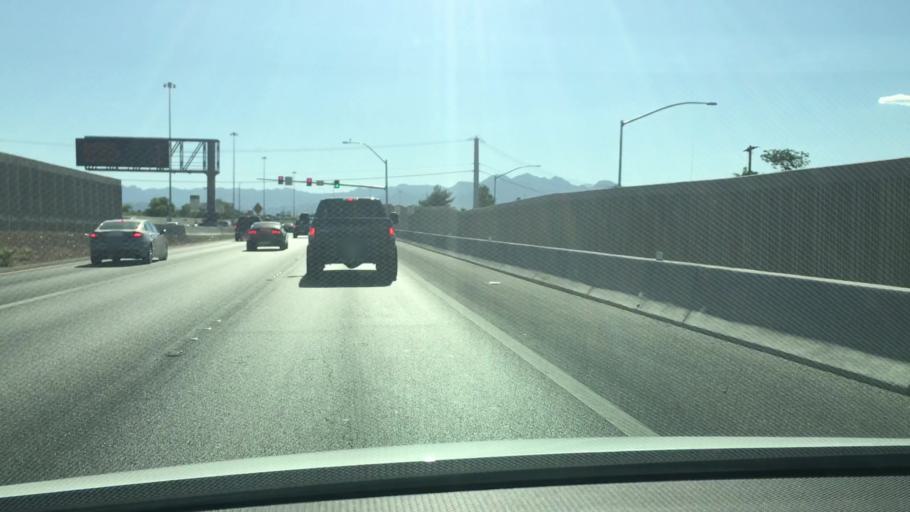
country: US
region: Nevada
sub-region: Clark County
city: Las Vegas
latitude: 36.1757
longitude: -115.1773
